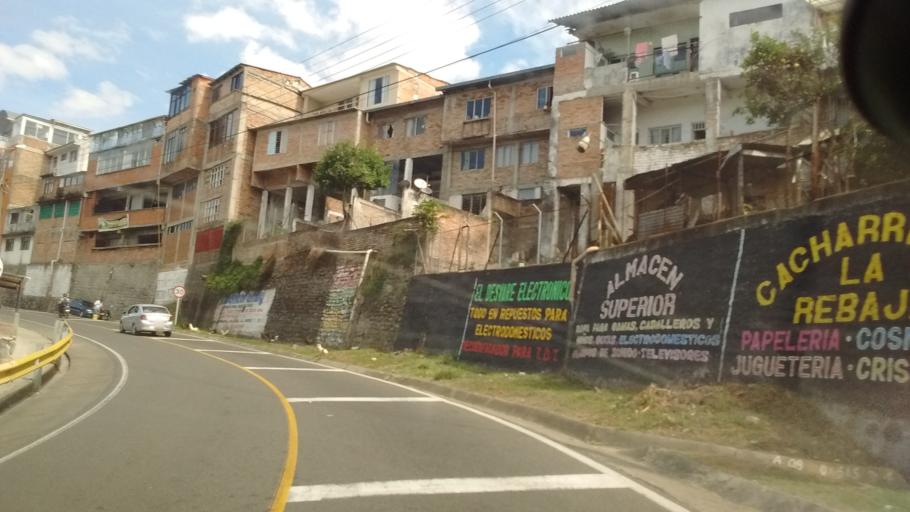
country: CO
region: Cauca
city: Cajibio
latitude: 2.6387
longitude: -76.5281
